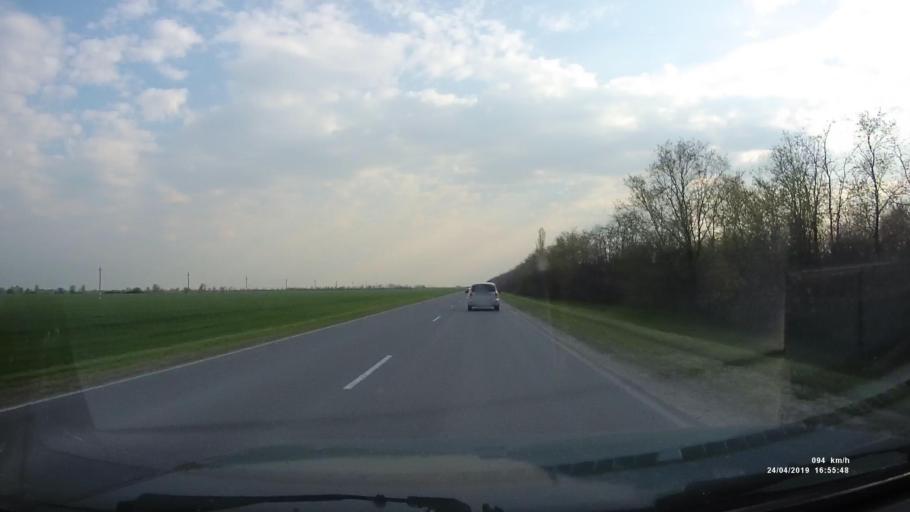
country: RU
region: Rostov
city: Proletarsk
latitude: 46.6595
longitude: 41.6843
